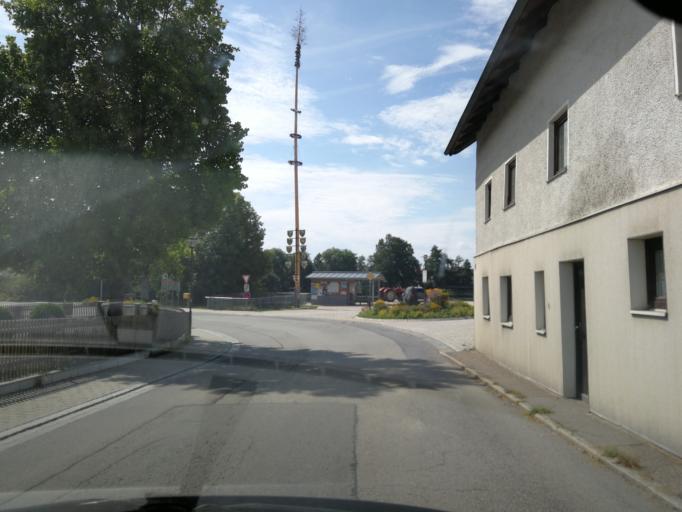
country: DE
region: Bavaria
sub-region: Lower Bavaria
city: Wiesenfelden
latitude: 49.0413
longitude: 12.5392
